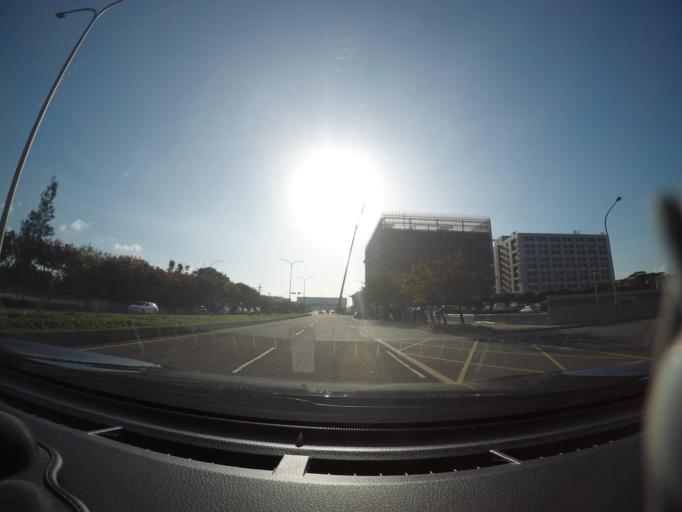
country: TW
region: Taiwan
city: Taoyuan City
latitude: 25.0935
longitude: 121.2568
